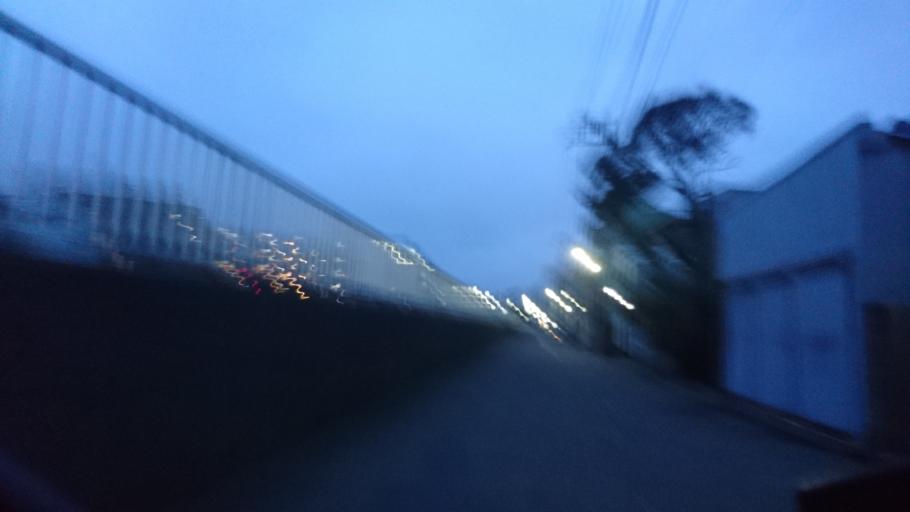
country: JP
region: Kanagawa
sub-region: Kawasaki-shi
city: Kawasaki
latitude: 35.5609
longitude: 139.7322
